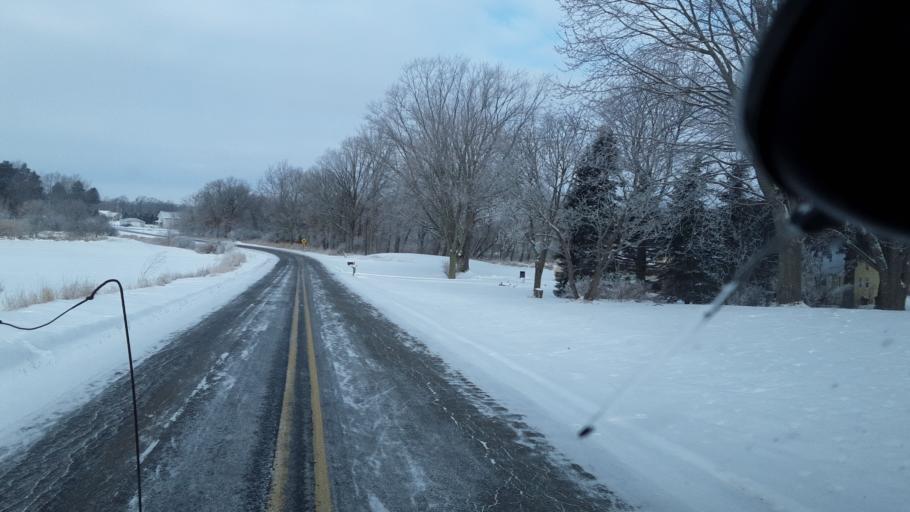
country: US
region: Michigan
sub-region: Ingham County
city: Leslie
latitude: 42.3710
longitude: -84.4888
